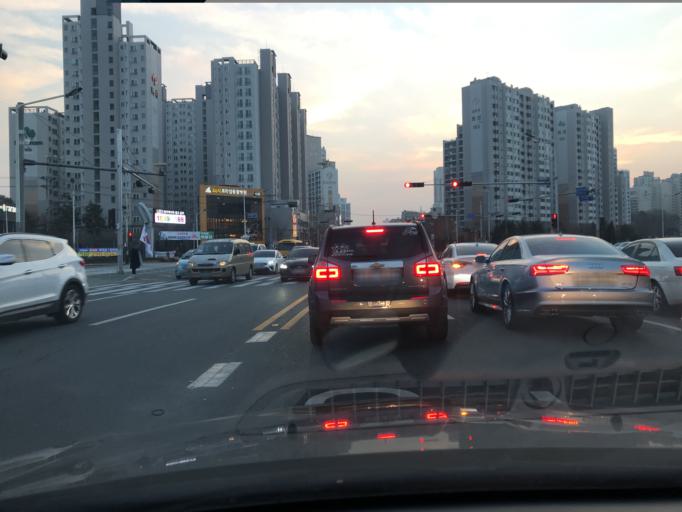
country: KR
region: Daegu
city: Hwawon
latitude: 35.8111
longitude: 128.5163
